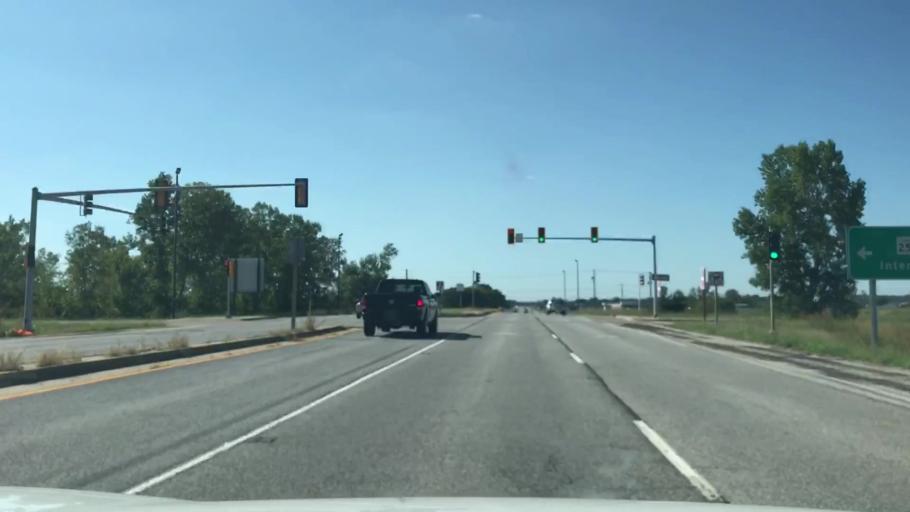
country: US
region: Illinois
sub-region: Madison County
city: Roxana
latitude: 38.8512
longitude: -90.0532
